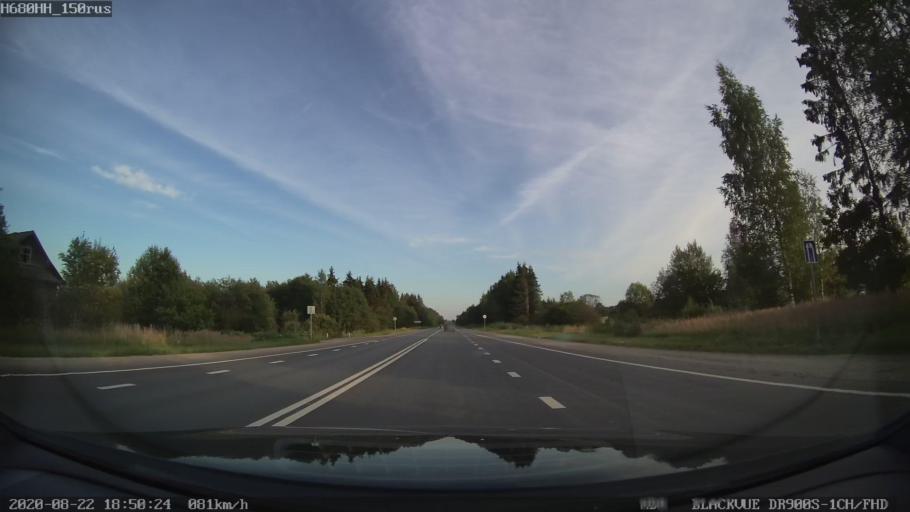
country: RU
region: Tverskaya
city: Rameshki
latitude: 57.2670
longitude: 36.0740
